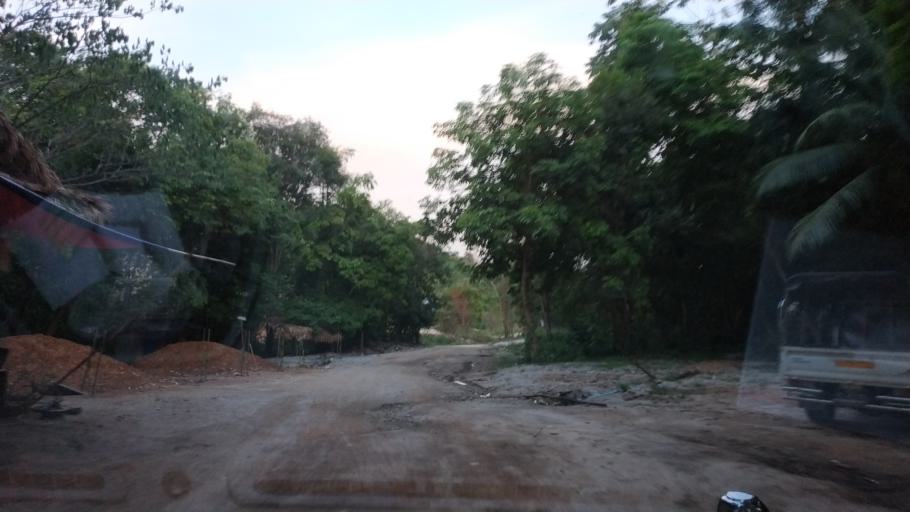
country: MM
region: Mon
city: Kyaikto
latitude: 17.4362
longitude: 97.0398
